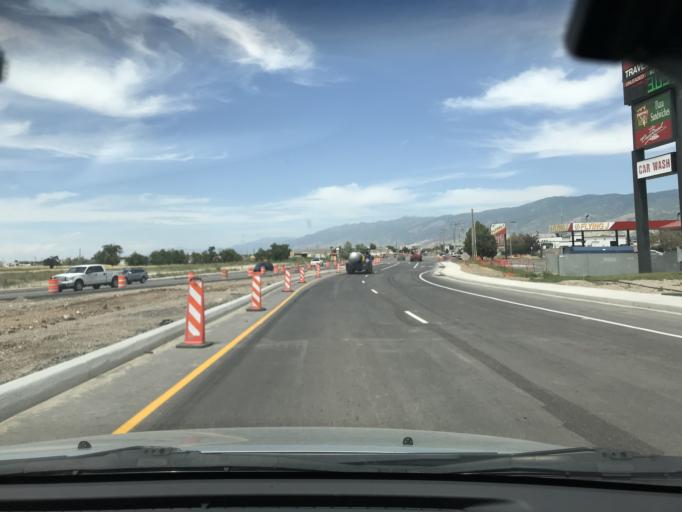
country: US
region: Utah
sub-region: Davis County
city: North Salt Lake
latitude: 40.8357
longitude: -111.9350
